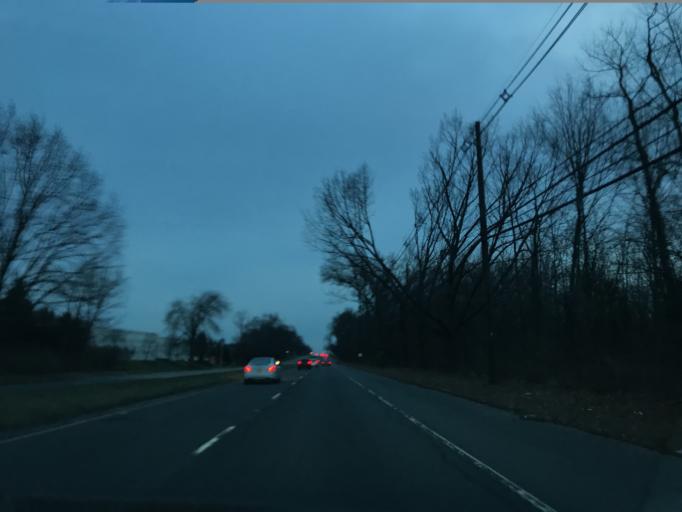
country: US
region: New Jersey
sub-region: Middlesex County
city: Cranbury
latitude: 40.3266
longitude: -74.5069
